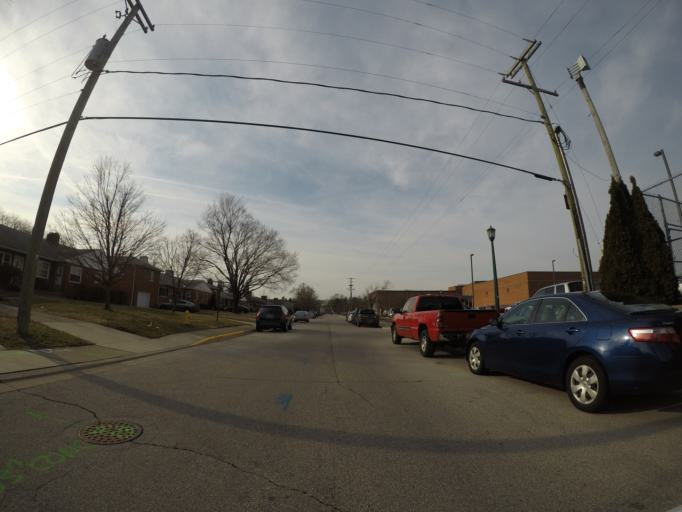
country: US
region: Ohio
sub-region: Franklin County
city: Upper Arlington
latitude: 40.0166
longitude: -83.0531
